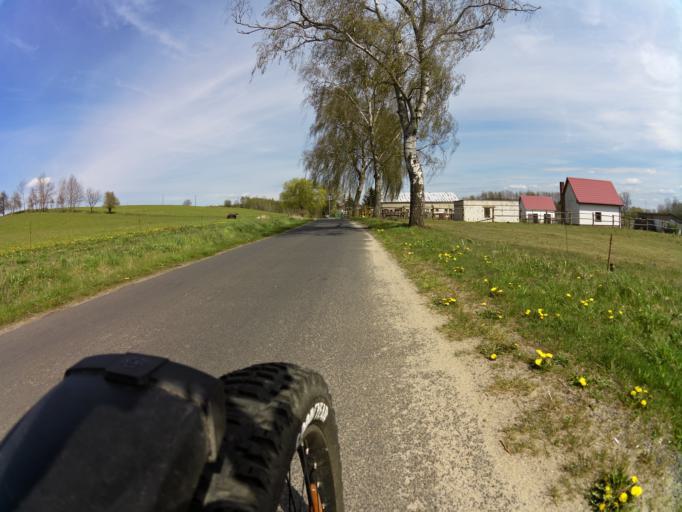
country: PL
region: West Pomeranian Voivodeship
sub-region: Powiat lobeski
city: Resko
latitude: 53.7802
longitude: 15.4166
